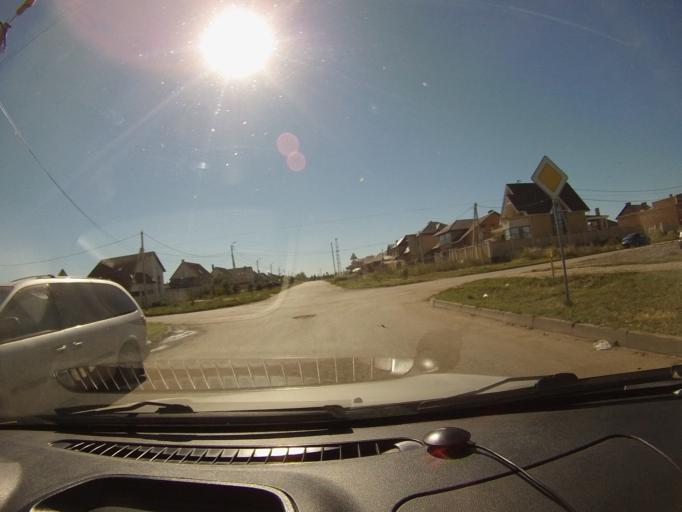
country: RU
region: Tambov
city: Tambov
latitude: 52.7684
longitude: 41.3816
